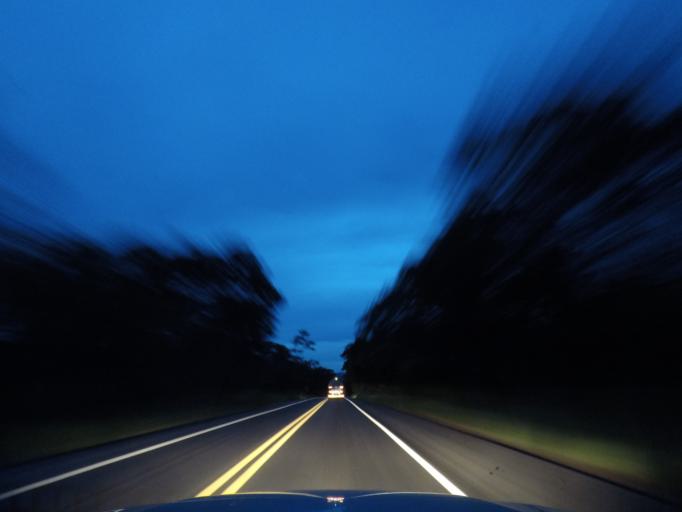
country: BR
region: Bahia
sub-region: Andarai
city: Vera Cruz
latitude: -12.4821
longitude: -41.3532
